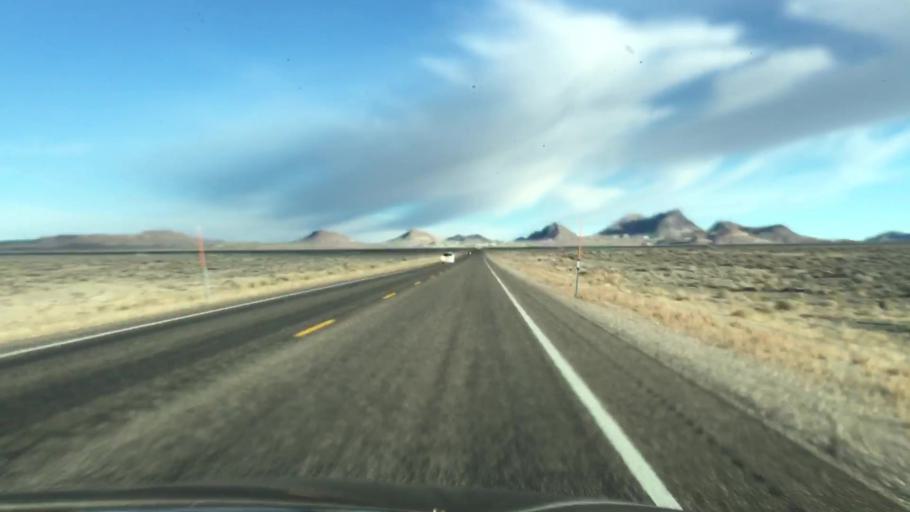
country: US
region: Nevada
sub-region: Nye County
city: Tonopah
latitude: 38.0982
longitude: -117.3228
